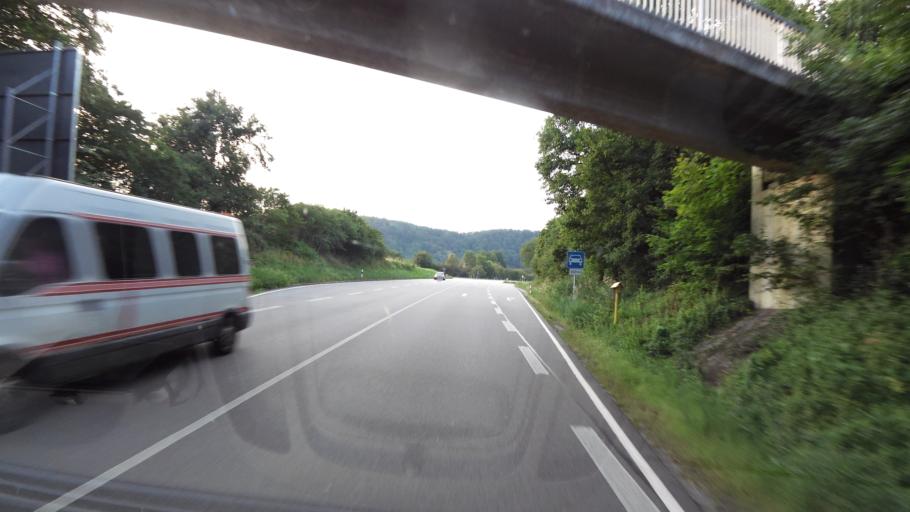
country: DE
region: Bavaria
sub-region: Lower Bavaria
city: Kirchdorf am Inn
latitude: 48.2568
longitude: 12.9983
